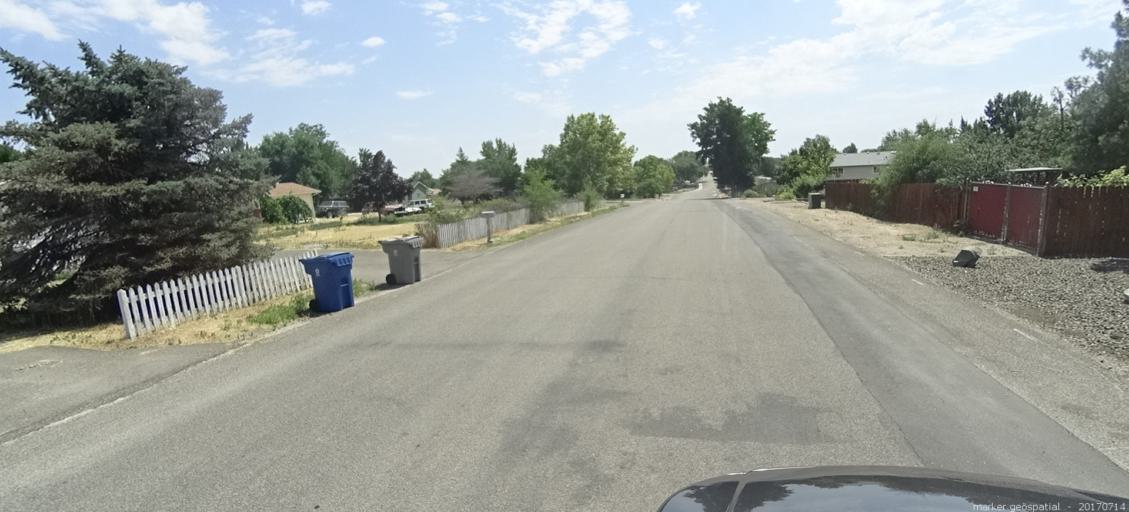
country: US
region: Idaho
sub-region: Ada County
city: Meridian
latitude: 43.5351
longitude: -116.3244
